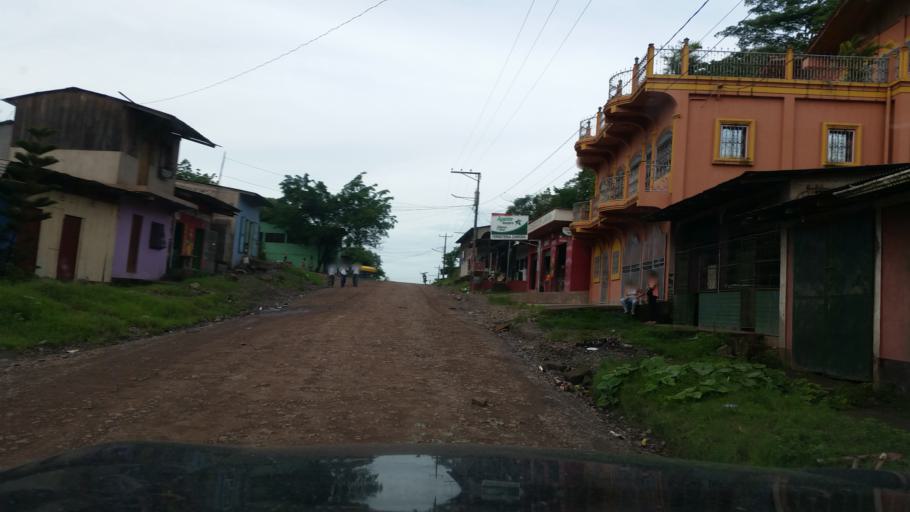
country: NI
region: Matagalpa
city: Rio Blanco
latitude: 13.1737
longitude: -84.9558
